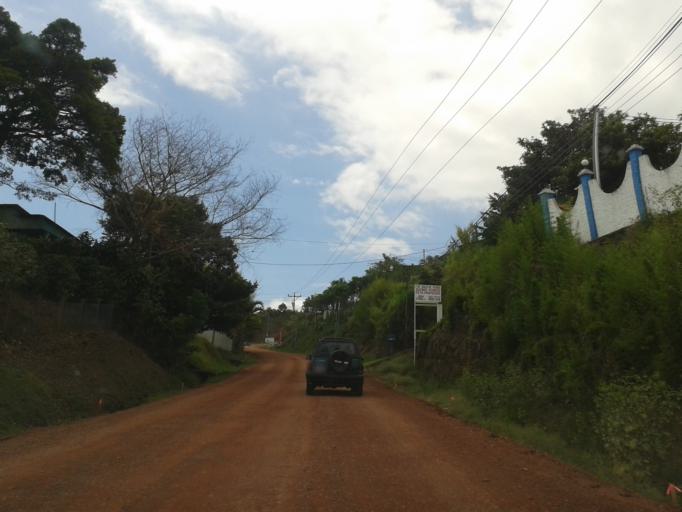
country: CR
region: Alajuela
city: Sabanilla
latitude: 10.0902
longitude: -84.1884
